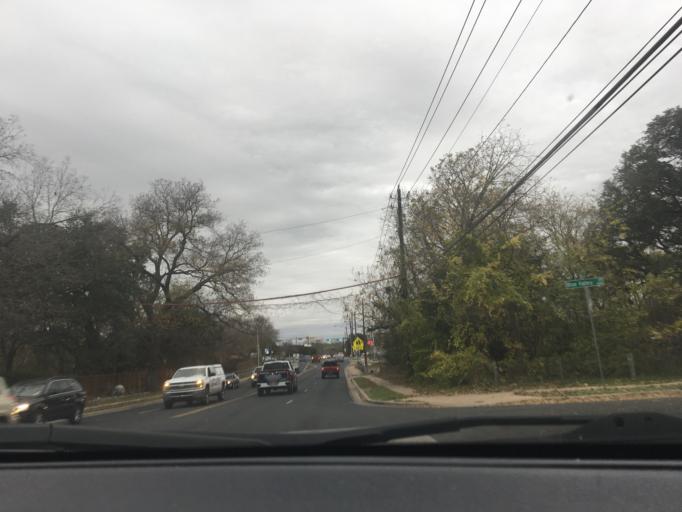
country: US
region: Texas
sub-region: Travis County
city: Onion Creek
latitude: 30.1828
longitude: -97.7935
